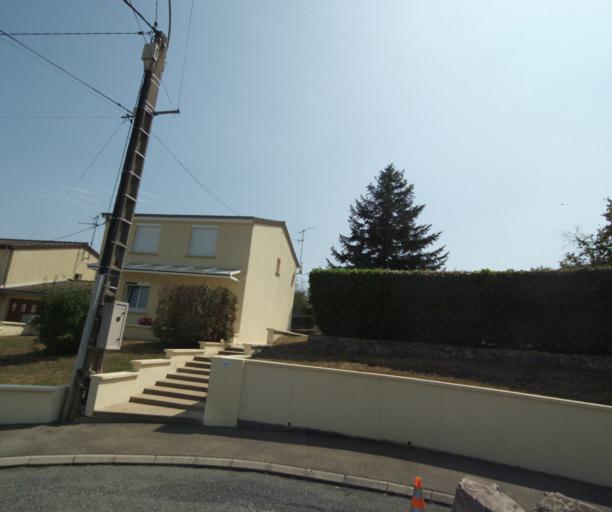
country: FR
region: Bourgogne
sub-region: Departement de Saone-et-Loire
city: Gueugnon
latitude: 46.5959
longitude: 4.0736
